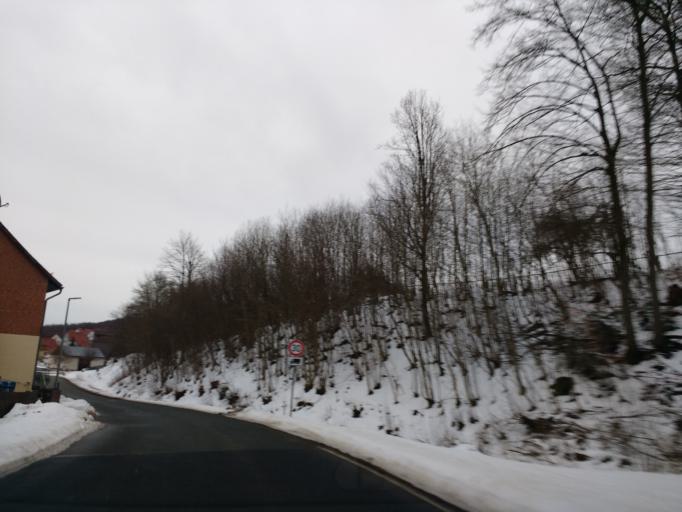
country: DE
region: Thuringia
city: Rohrberg
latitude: 51.4282
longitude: 10.0250
